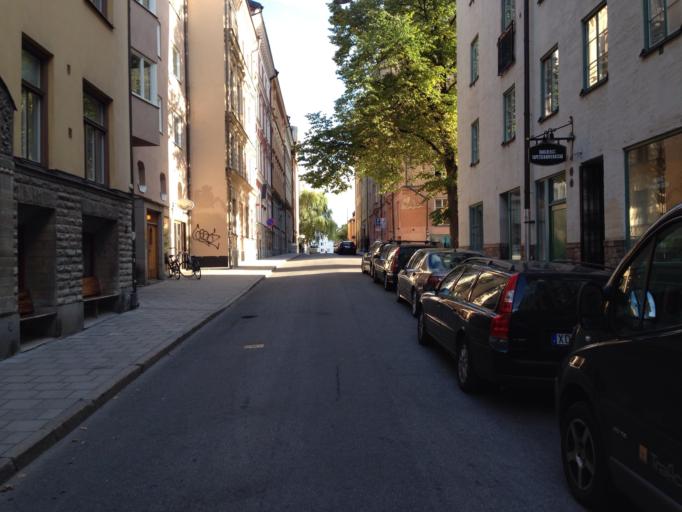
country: SE
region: Stockholm
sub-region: Stockholms Kommun
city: Stockholm
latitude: 59.3176
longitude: 18.0650
